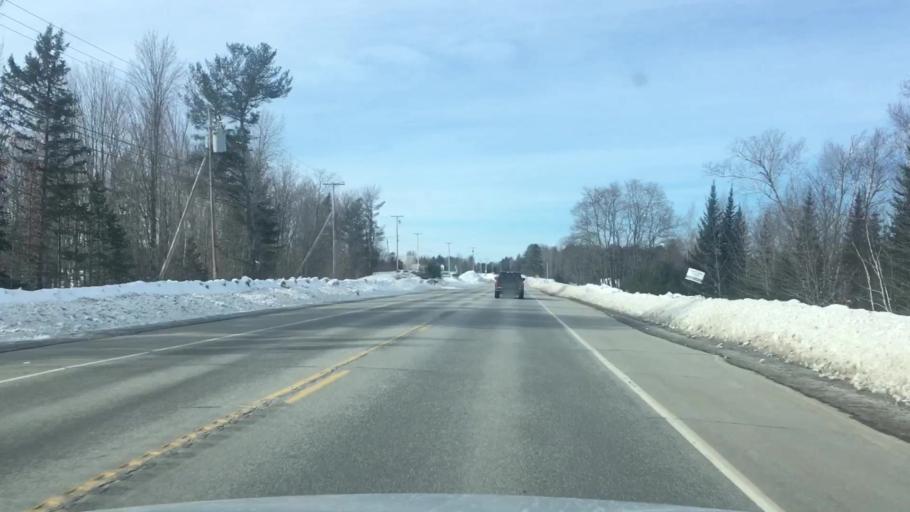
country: US
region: Maine
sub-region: Penobscot County
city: Kenduskeag
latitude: 44.9498
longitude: -68.9472
